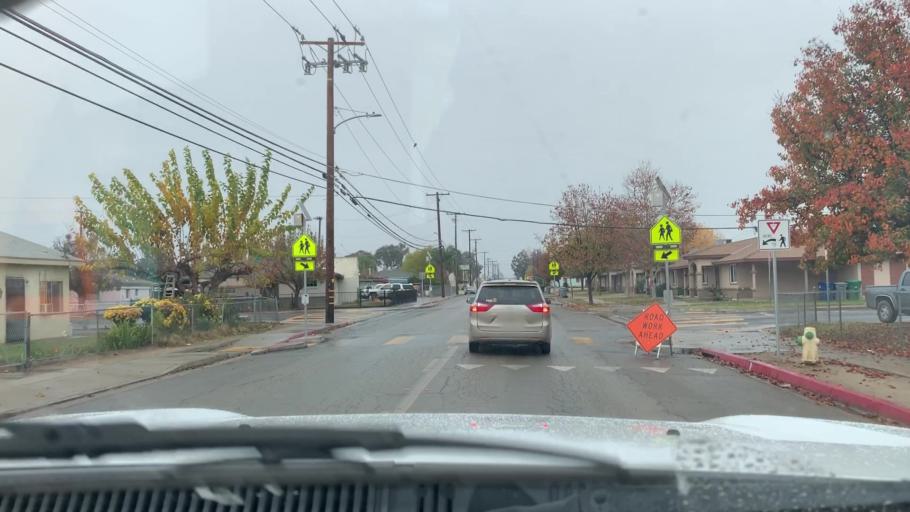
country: US
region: California
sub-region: Kern County
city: Delano
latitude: 35.7614
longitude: -119.2527
